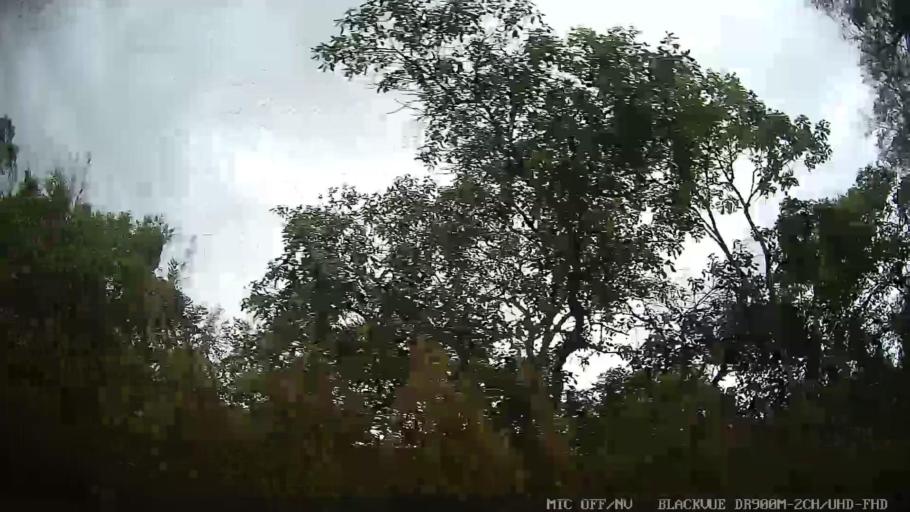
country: BR
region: Sao Paulo
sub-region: Itatiba
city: Itatiba
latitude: -23.0360
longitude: -46.8945
